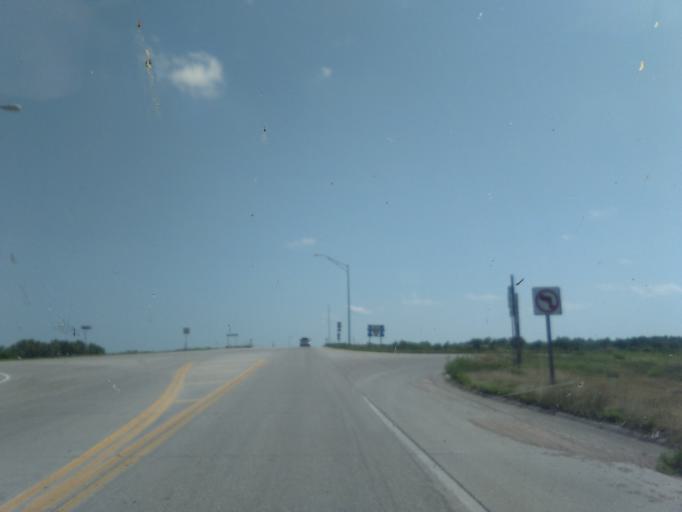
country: US
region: Nebraska
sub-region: Phelps County
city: Holdrege
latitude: 40.6920
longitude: -99.3799
